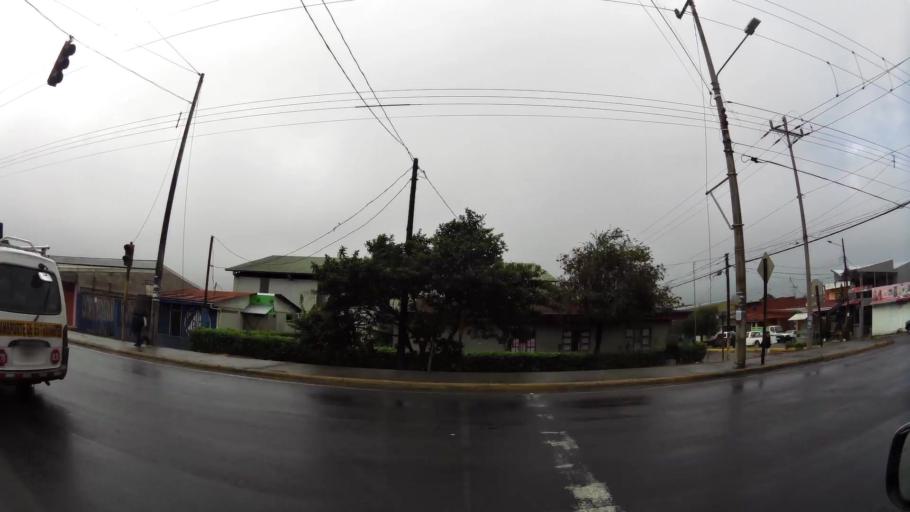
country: CR
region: Cartago
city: Paraiso
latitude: 9.8405
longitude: -83.8771
